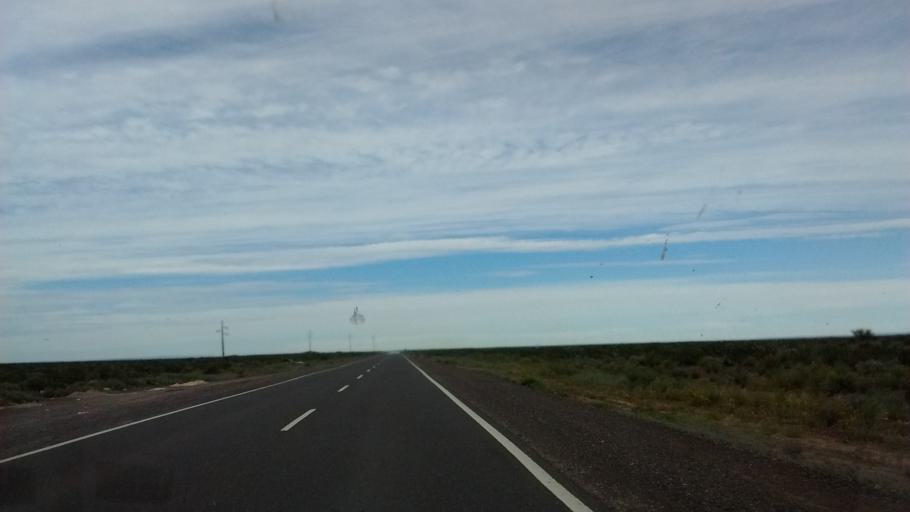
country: AR
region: Rio Negro
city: Contraalmirante Cordero
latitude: -38.6360
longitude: -68.1311
